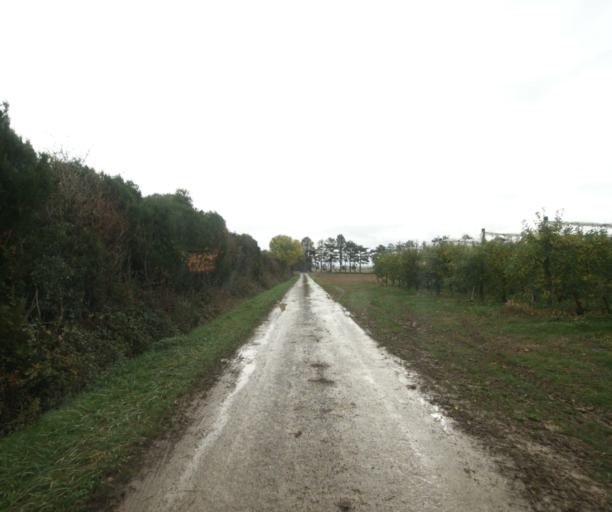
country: FR
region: Rhone-Alpes
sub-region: Departement de l'Ain
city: Pont-de-Vaux
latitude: 46.4828
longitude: 4.8856
